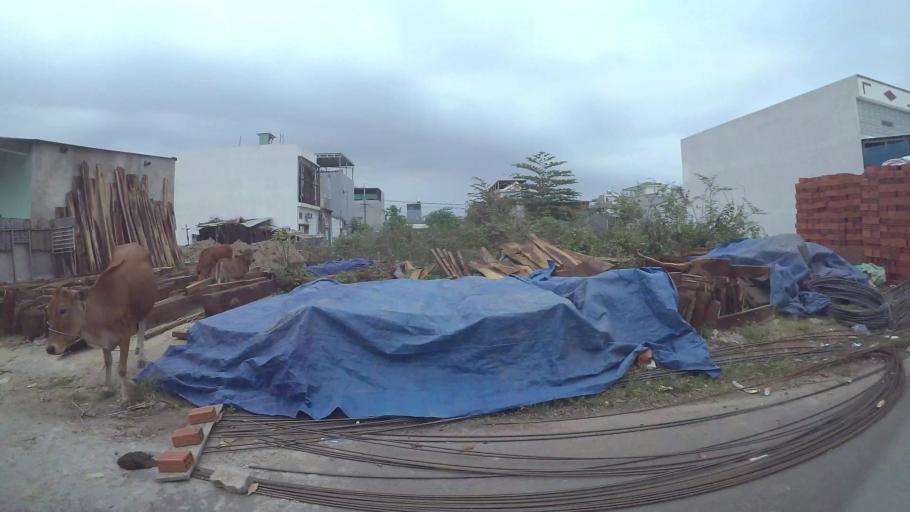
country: VN
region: Da Nang
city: Lien Chieu
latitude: 16.0437
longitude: 108.1682
